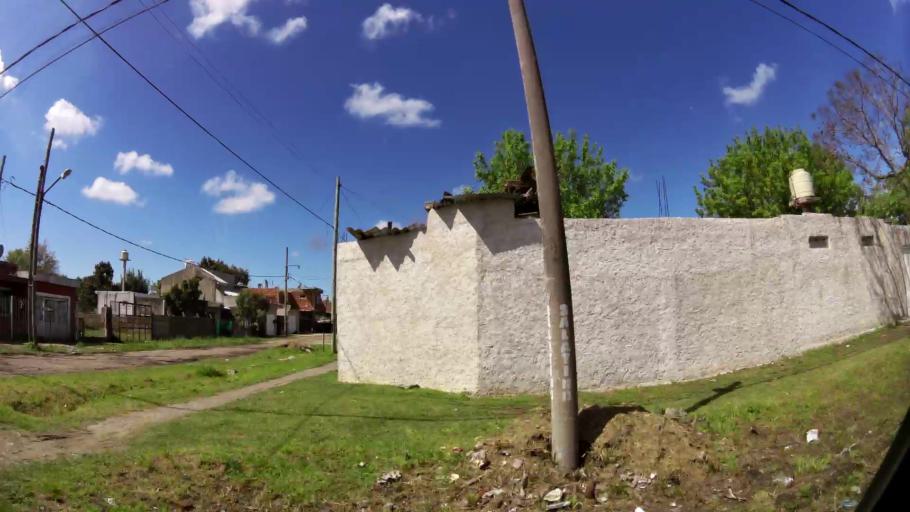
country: AR
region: Buenos Aires
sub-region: Partido de Quilmes
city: Quilmes
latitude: -34.8187
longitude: -58.2569
